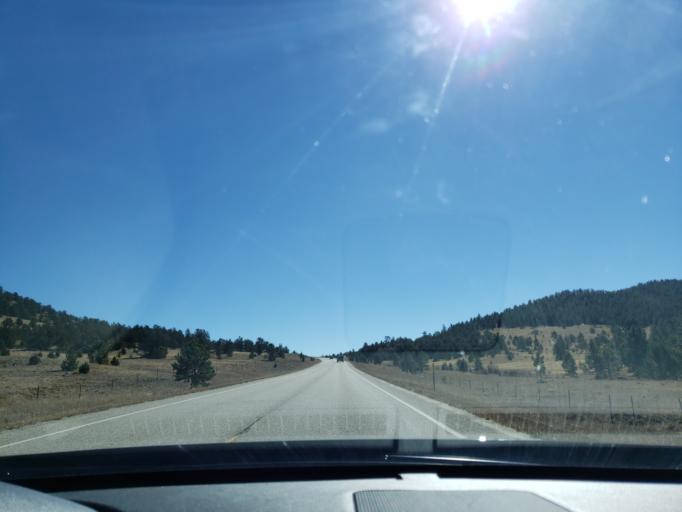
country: US
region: Colorado
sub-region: Chaffee County
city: Salida
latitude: 38.8429
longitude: -105.6412
